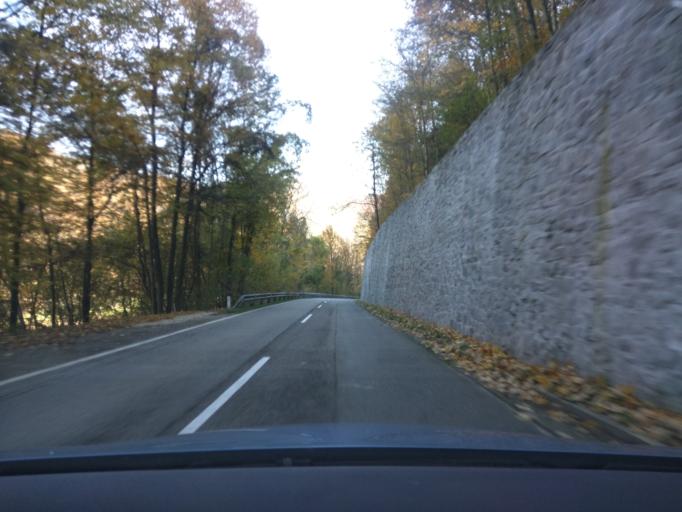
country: DE
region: Bavaria
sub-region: Lower Bavaria
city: Untergriesbach
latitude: 48.5142
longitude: 13.7145
